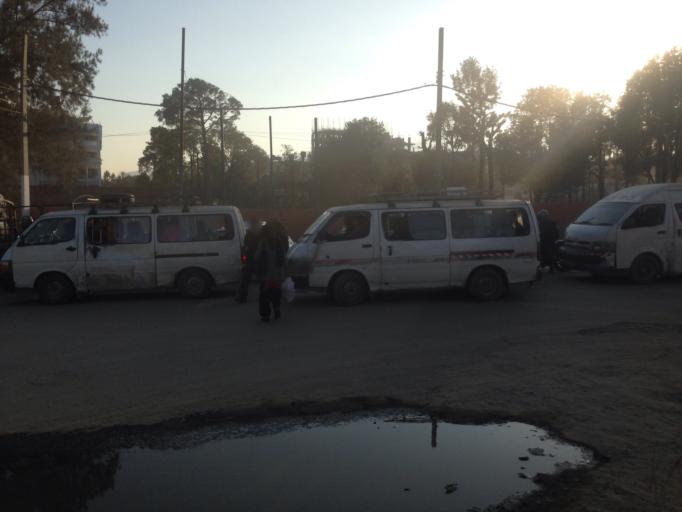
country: NP
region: Central Region
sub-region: Bagmati Zone
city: Kathmandu
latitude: 27.7172
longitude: 85.3160
